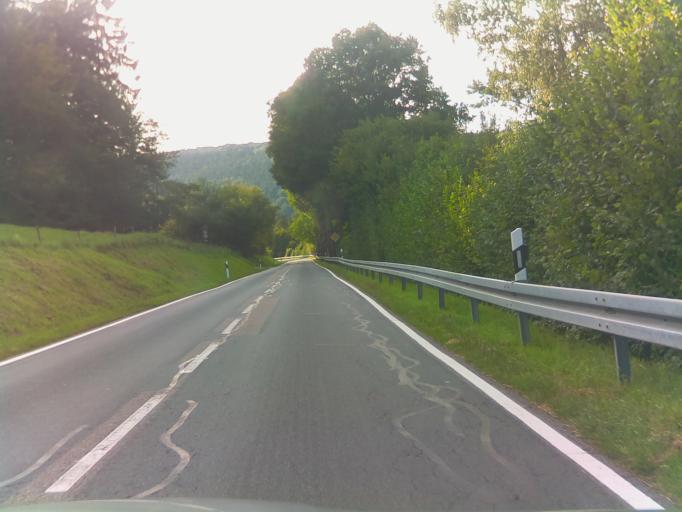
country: DE
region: Hesse
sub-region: Regierungsbezirk Darmstadt
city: Beerfelden
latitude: 49.5489
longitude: 8.9378
